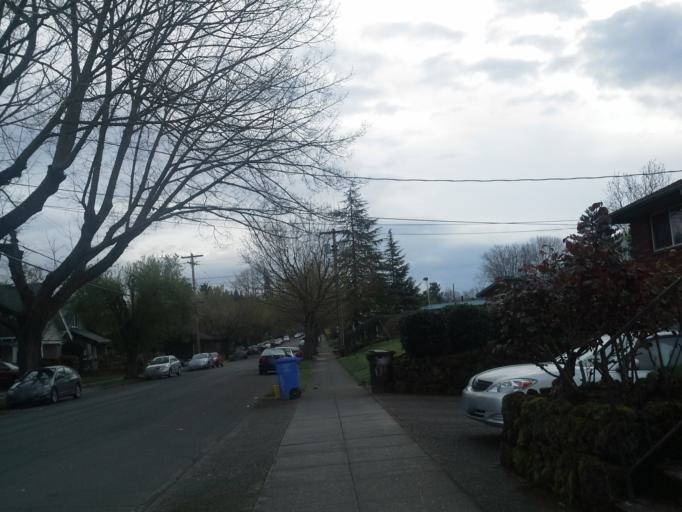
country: US
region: Oregon
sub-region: Clackamas County
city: Milwaukie
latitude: 45.4947
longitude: -122.6287
